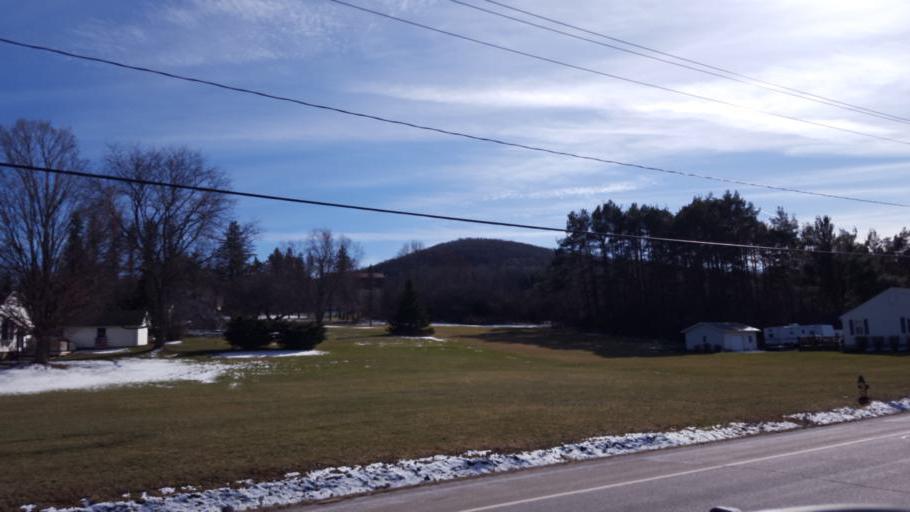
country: US
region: New York
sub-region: Allegany County
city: Wellsville
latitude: 42.1248
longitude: -77.9745
